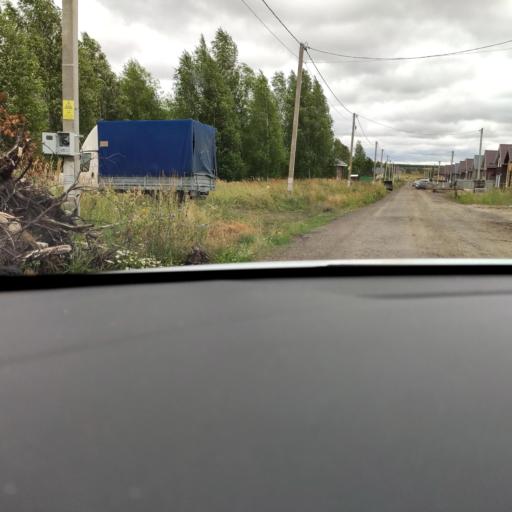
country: RU
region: Tatarstan
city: Stolbishchi
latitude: 55.7157
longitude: 49.3069
